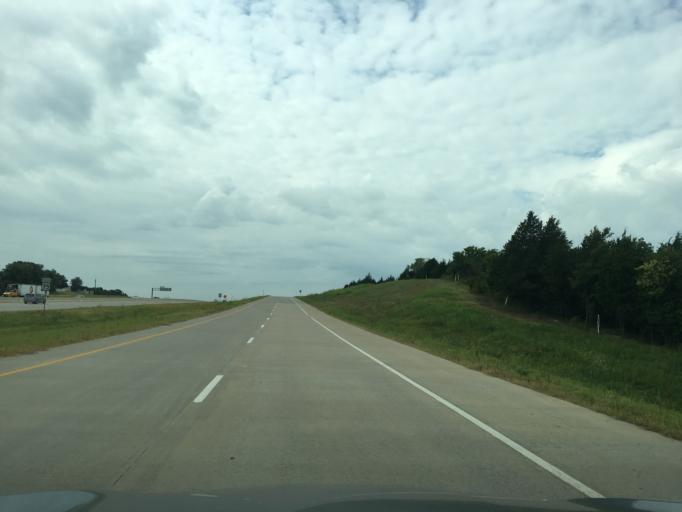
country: US
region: Texas
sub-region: Collin County
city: Melissa
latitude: 33.2985
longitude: -96.5921
